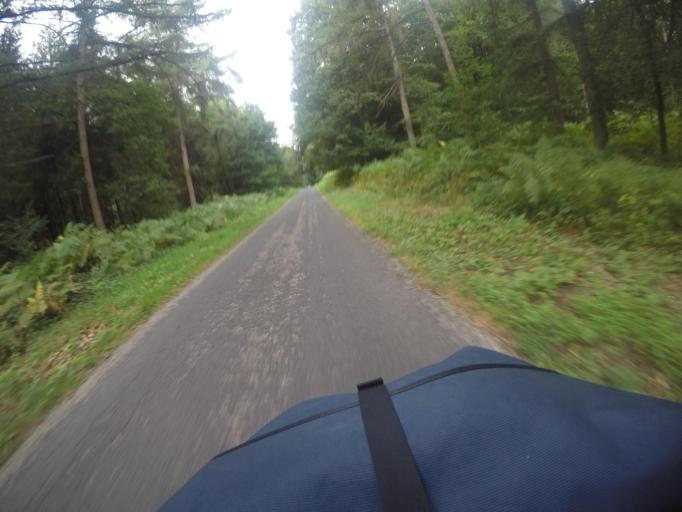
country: DE
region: North Rhine-Westphalia
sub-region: Regierungsbezirk Dusseldorf
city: Kranenburg
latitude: 51.7373
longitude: 6.0104
